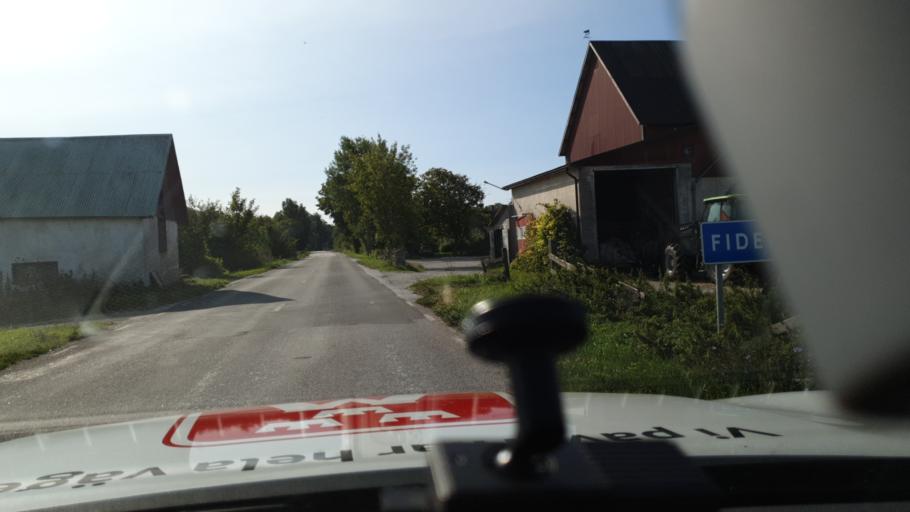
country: SE
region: Gotland
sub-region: Gotland
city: Hemse
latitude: 57.0975
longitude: 18.3036
